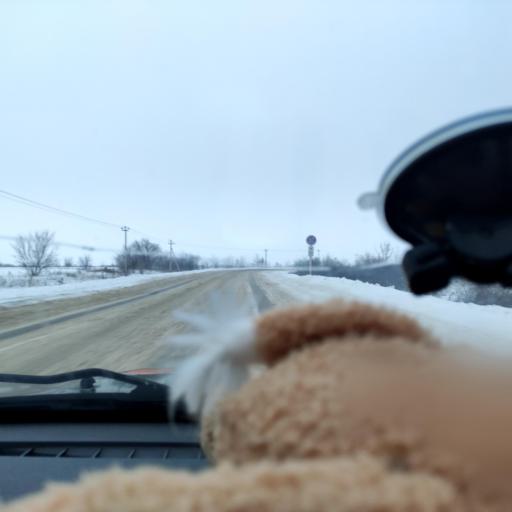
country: RU
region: Samara
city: Podstepki
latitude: 53.5249
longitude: 49.0836
